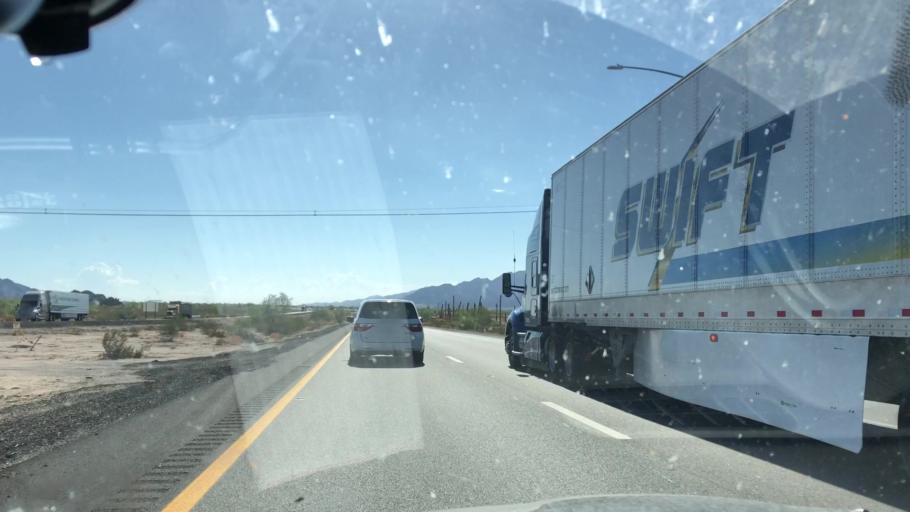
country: US
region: California
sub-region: Imperial County
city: Niland
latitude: 33.7106
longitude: -115.4043
